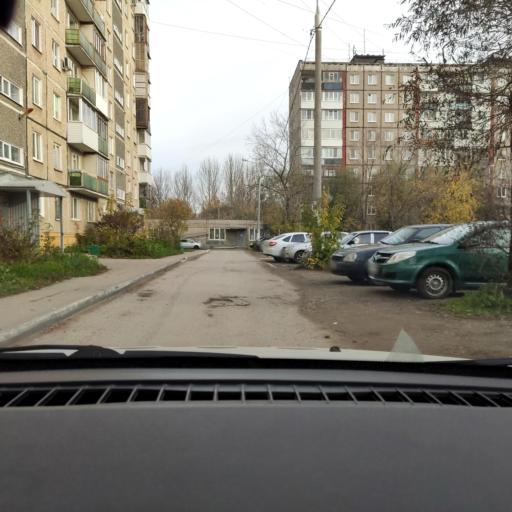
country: RU
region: Perm
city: Perm
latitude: 58.0633
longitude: 56.3476
